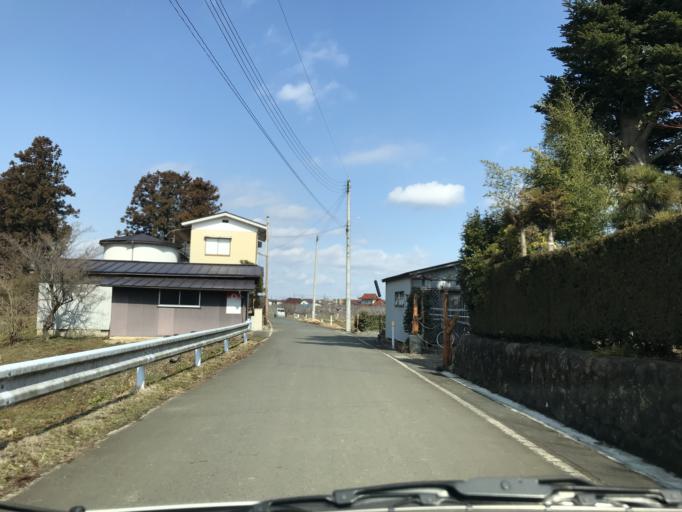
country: JP
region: Iwate
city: Mizusawa
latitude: 39.0406
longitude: 141.1391
